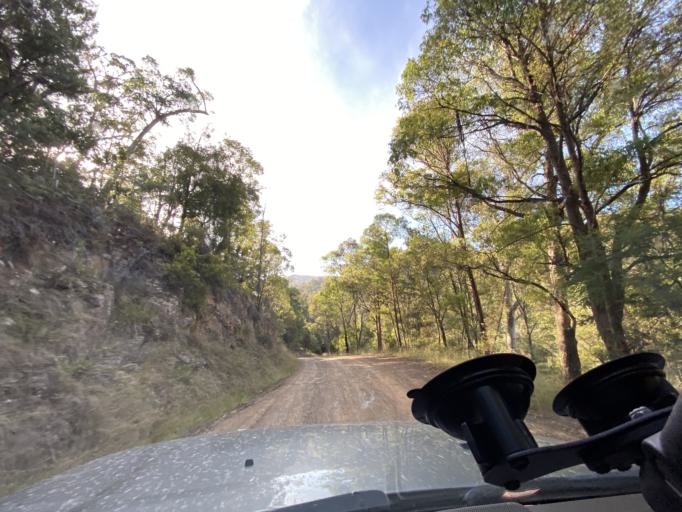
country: AU
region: Victoria
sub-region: Mansfield
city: Mansfield
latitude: -37.5216
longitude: 146.0780
